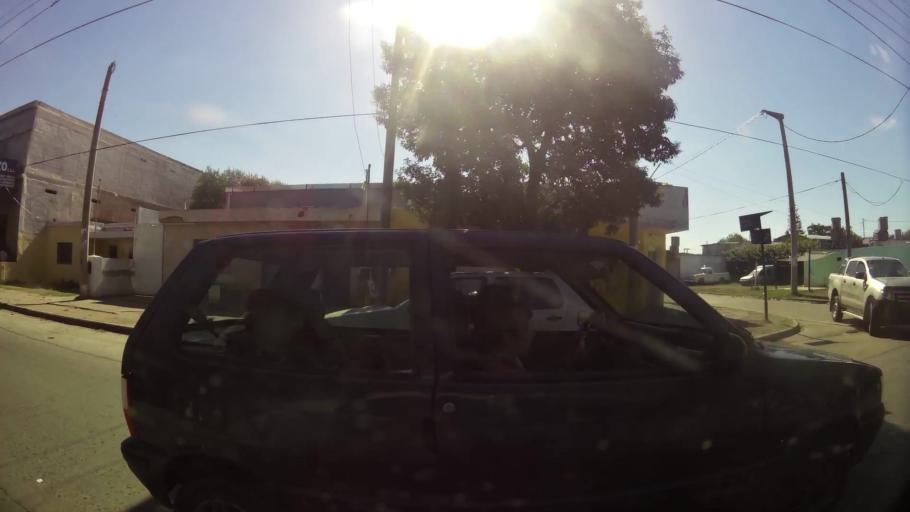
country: AR
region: Cordoba
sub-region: Departamento de Capital
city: Cordoba
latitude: -31.3675
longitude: -64.1840
